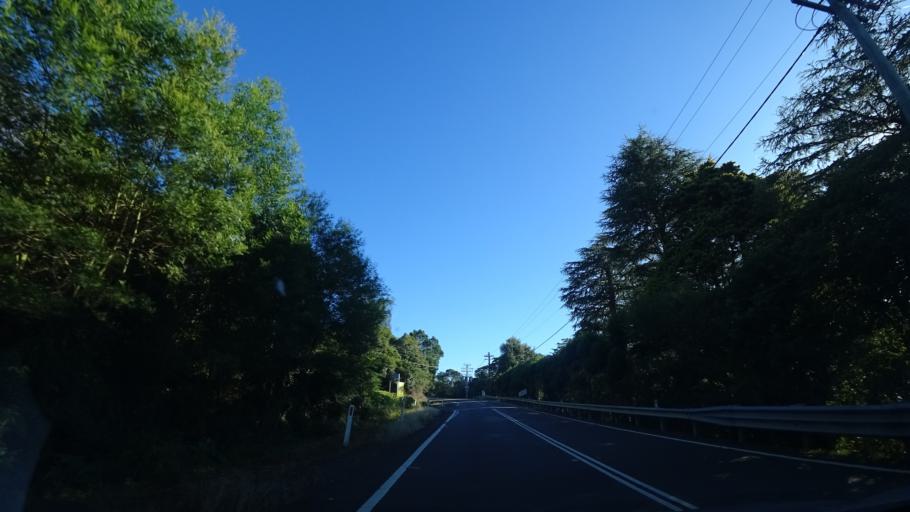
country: AU
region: New South Wales
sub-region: Hawkesbury
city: Richmond
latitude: -33.5262
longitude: 150.6291
